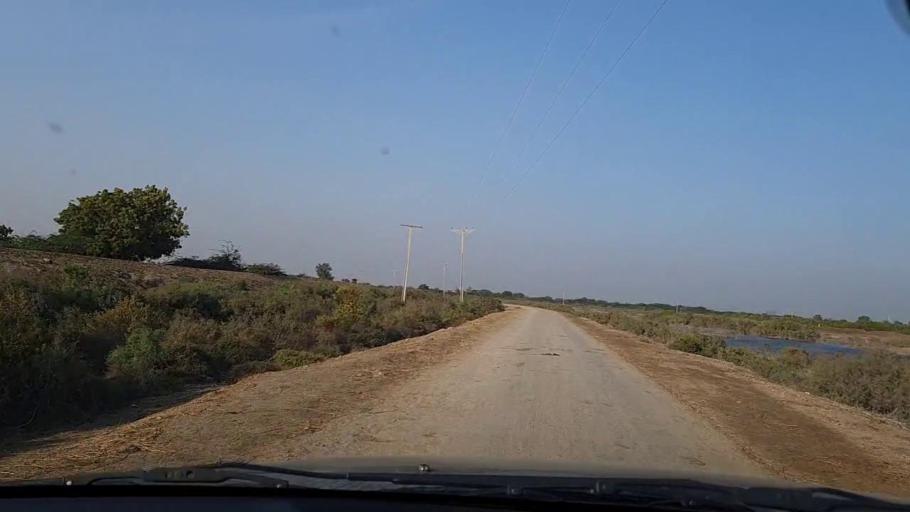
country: PK
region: Sindh
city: Chuhar Jamali
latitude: 24.2906
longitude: 67.7548
